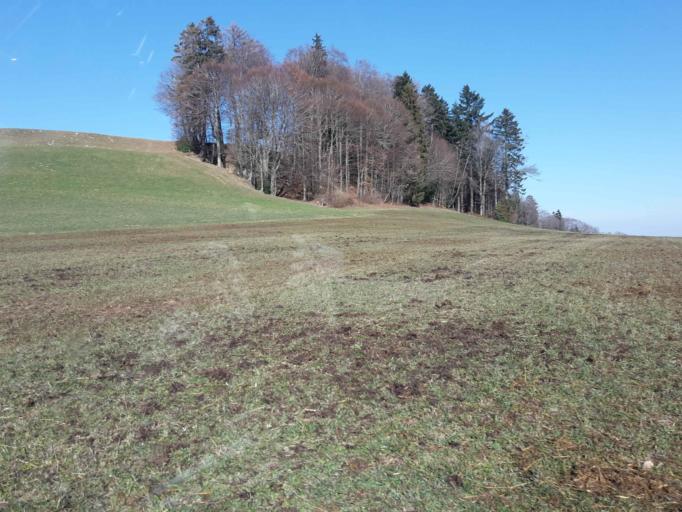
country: CH
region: Bern
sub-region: Emmental District
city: Durrenroth
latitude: 47.1150
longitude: 7.7900
